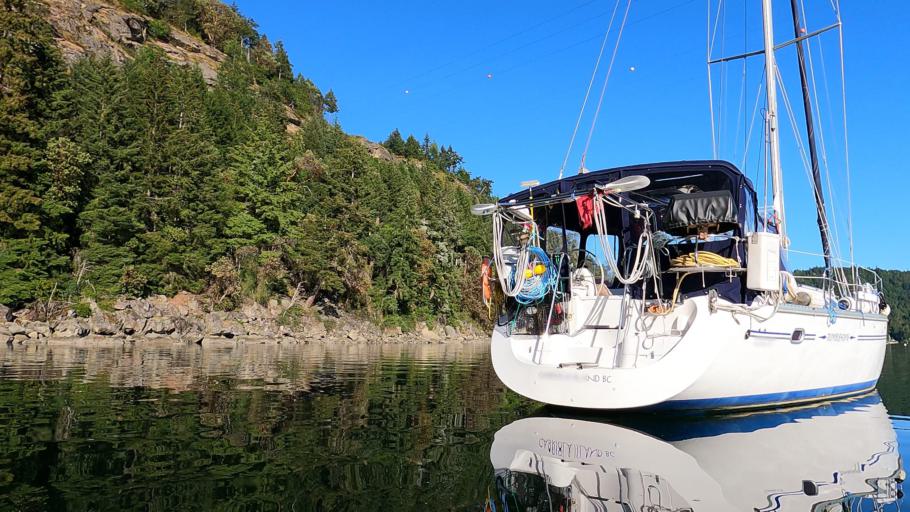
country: CA
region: British Columbia
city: North Saanich
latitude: 48.8972
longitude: -123.4001
